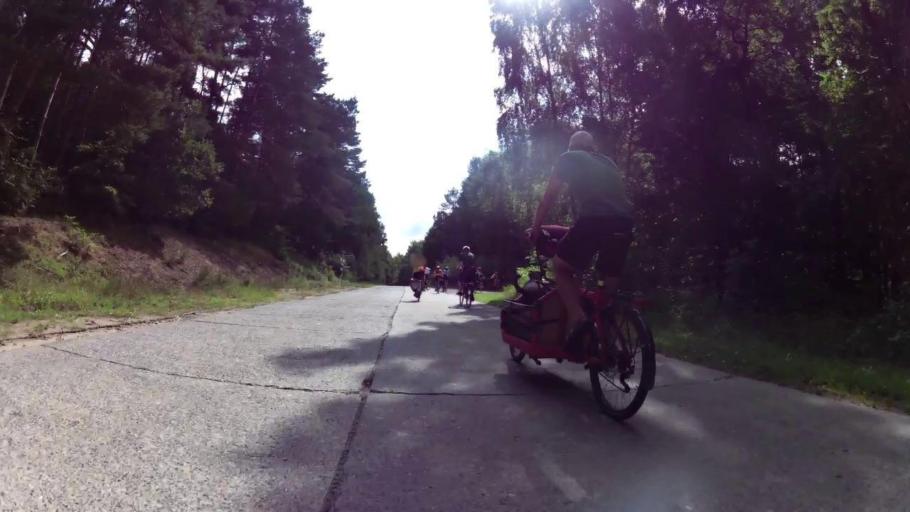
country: PL
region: West Pomeranian Voivodeship
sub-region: Powiat drawski
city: Drawsko Pomorskie
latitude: 53.4730
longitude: 15.7845
